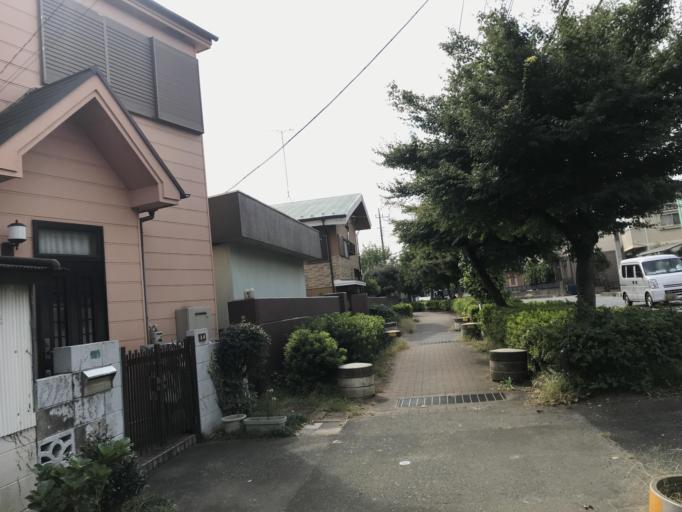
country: JP
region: Tokyo
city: Tanashicho
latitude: 35.7750
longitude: 139.5415
